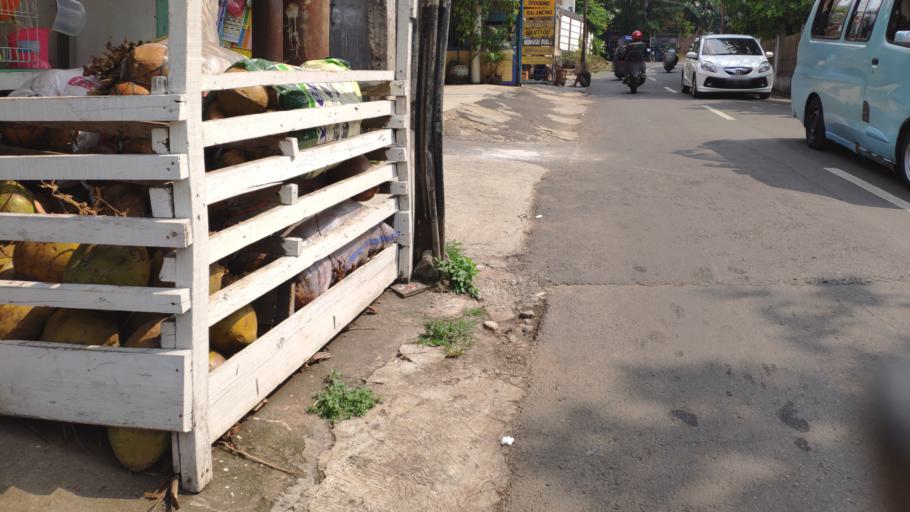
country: ID
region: West Java
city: Depok
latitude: -6.3187
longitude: 106.8190
